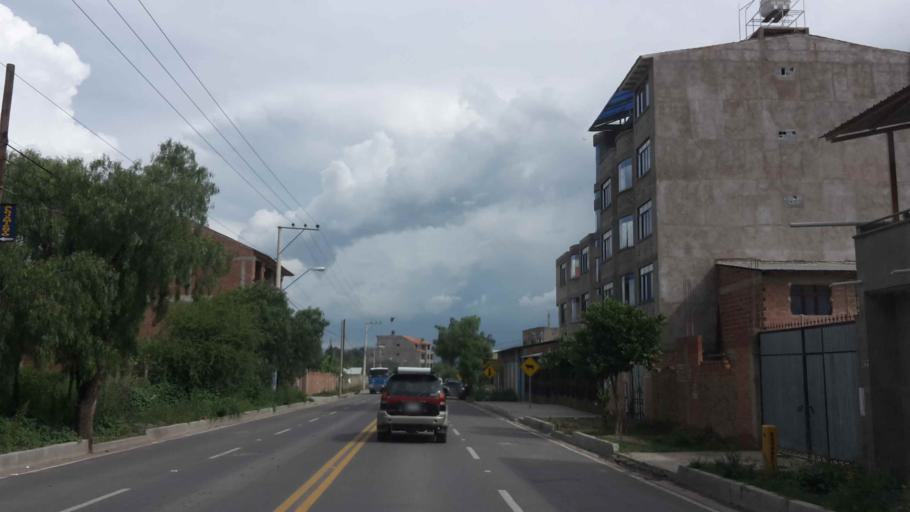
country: BO
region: Cochabamba
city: Cochabamba
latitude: -17.3516
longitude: -66.2560
